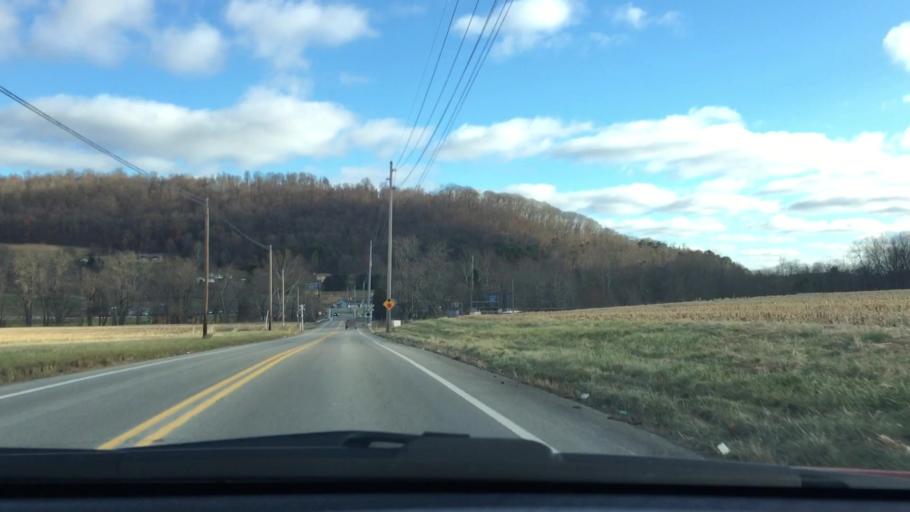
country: US
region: Pennsylvania
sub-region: Indiana County
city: Indiana
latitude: 40.6560
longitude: -79.3076
